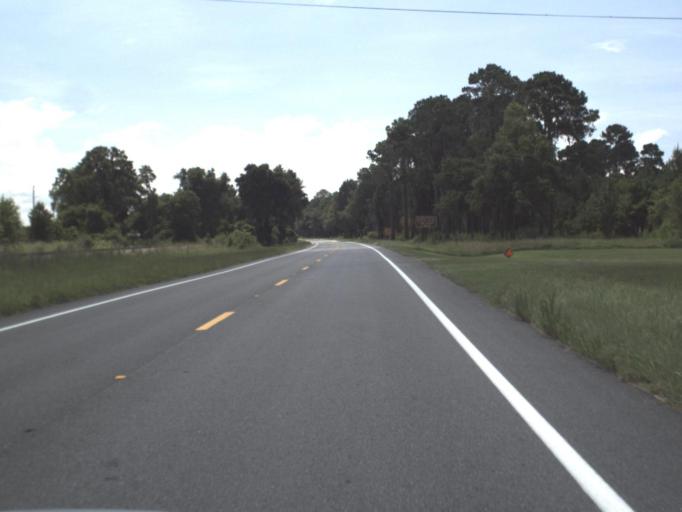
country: US
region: Florida
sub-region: Suwannee County
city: Wellborn
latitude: 30.3901
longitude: -82.8248
